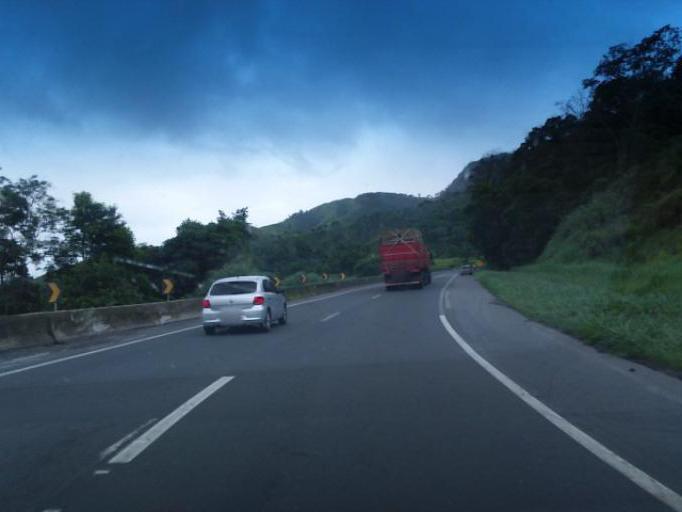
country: BR
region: Sao Paulo
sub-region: Cajati
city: Cajati
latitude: -24.8563
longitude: -48.2123
